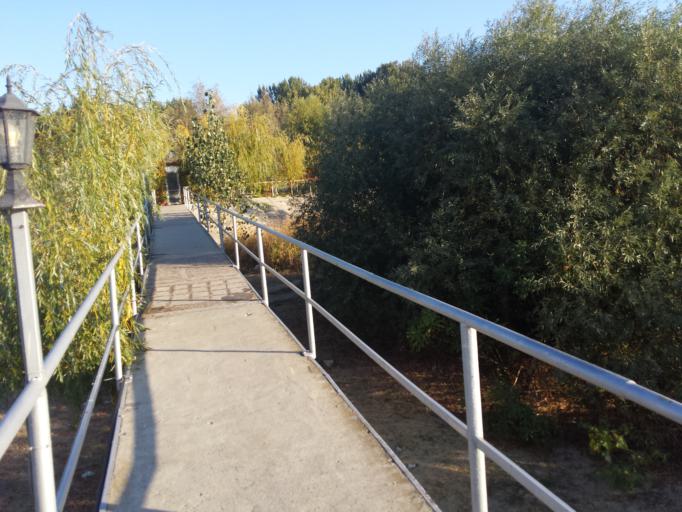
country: BG
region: Pleven
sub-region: Obshtina Nikopol
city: Nikopol
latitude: 43.7122
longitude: 24.8882
